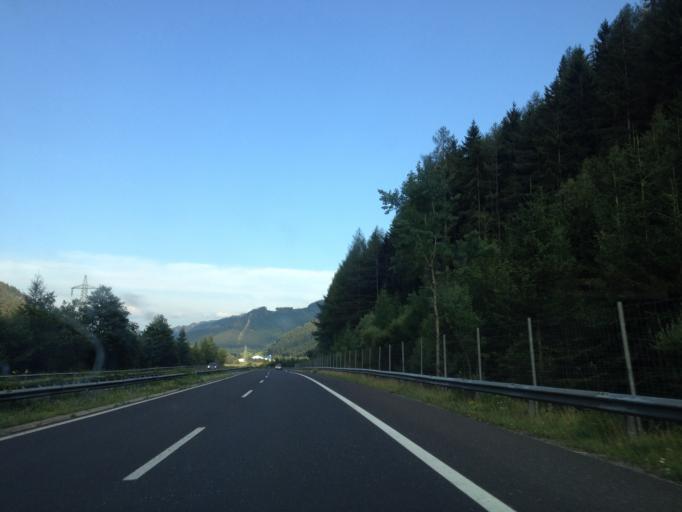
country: AT
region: Styria
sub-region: Politischer Bezirk Leoben
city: Kalwang
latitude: 47.4041
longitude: 14.7798
